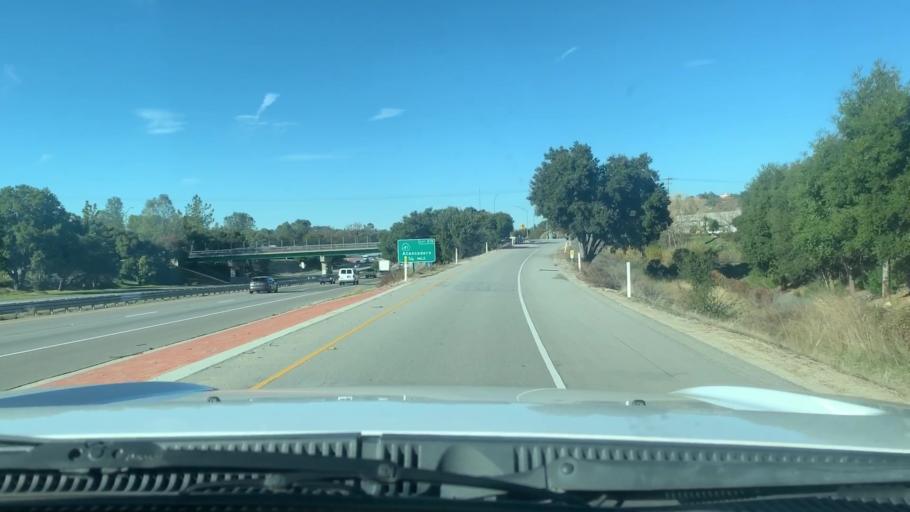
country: US
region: California
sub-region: San Luis Obispo County
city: Atascadero
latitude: 35.4753
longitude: -120.6575
